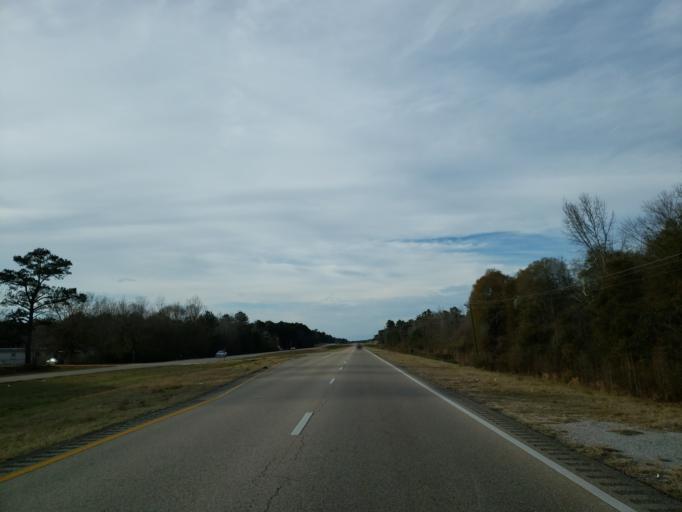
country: US
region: Mississippi
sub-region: Wayne County
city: Waynesboro
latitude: 31.6139
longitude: -88.5725
